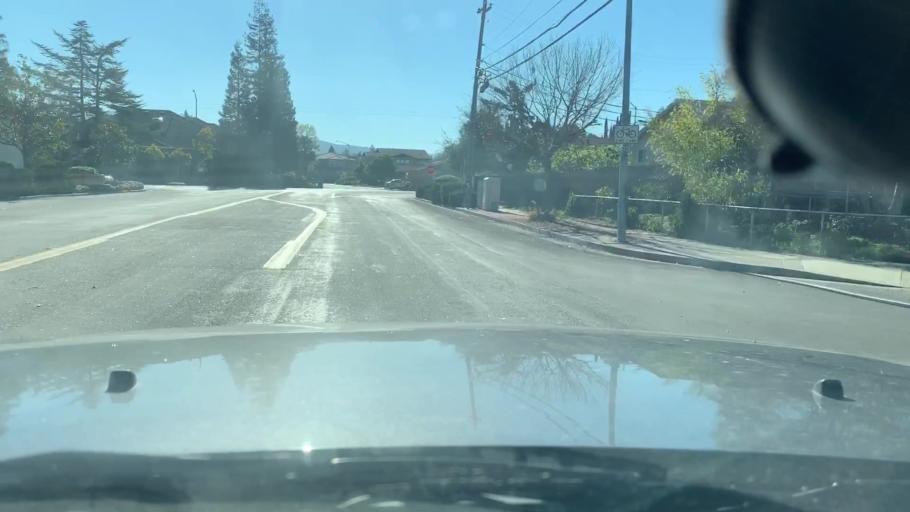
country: US
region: California
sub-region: Santa Clara County
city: Campbell
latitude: 37.2724
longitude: -121.9765
